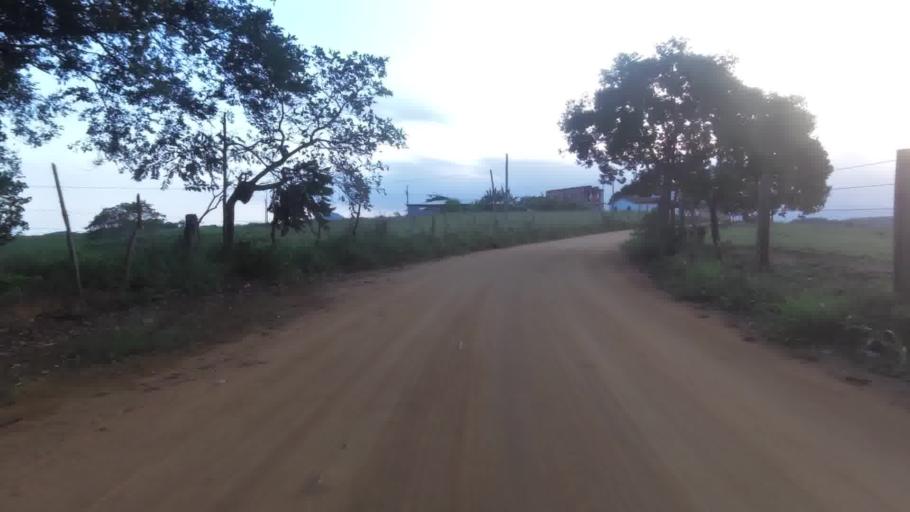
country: BR
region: Espirito Santo
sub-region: Guarapari
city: Guarapari
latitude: -20.7003
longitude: -40.5744
